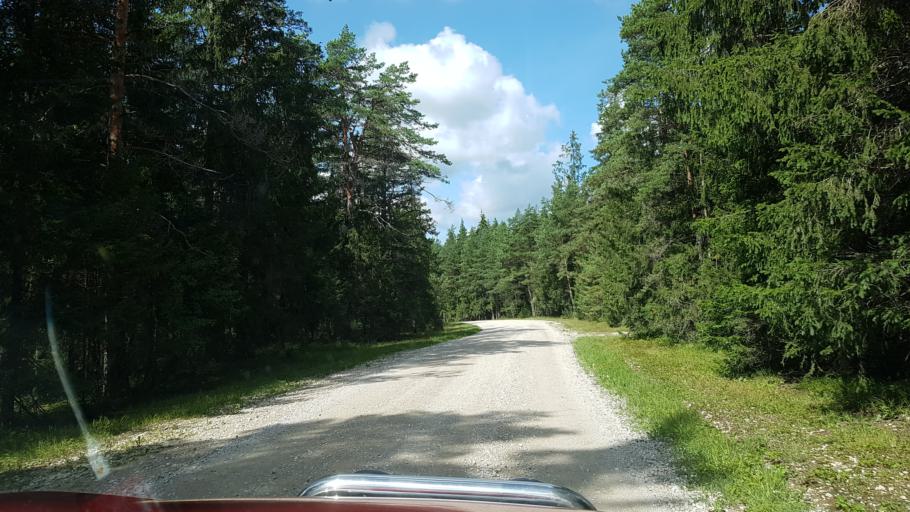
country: EE
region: Raplamaa
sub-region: Rapla vald
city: Rapla
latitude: 58.9650
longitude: 24.6367
